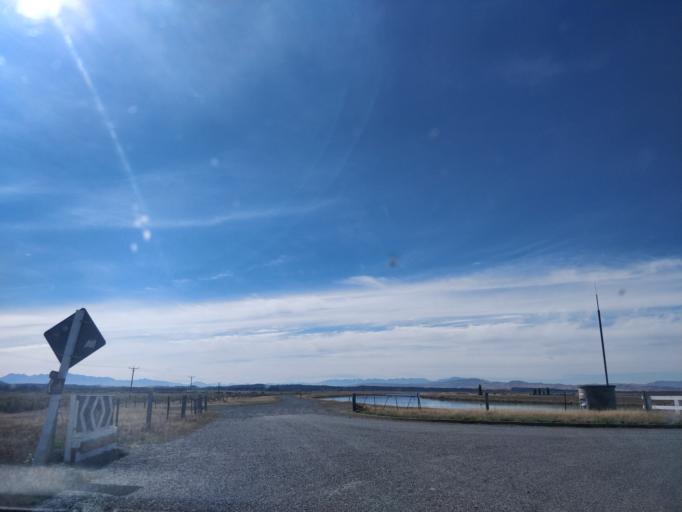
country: NZ
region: Otago
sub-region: Queenstown-Lakes District
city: Wanaka
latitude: -44.2200
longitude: 170.0500
